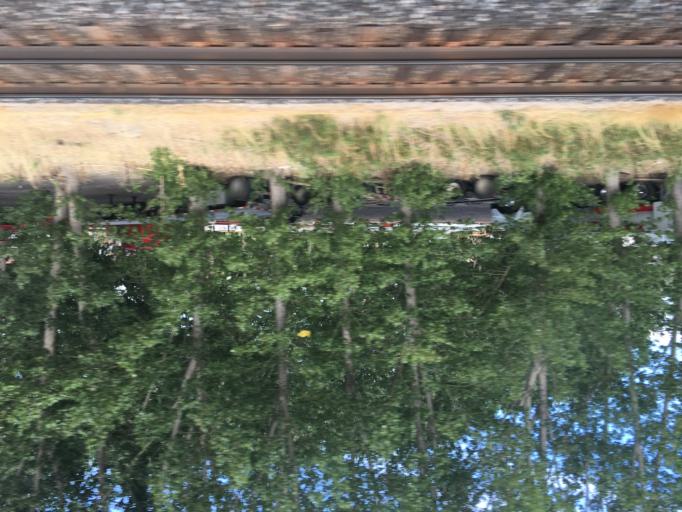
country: US
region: Utah
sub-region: Utah County
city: Lehi
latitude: 40.3933
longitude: -111.8591
